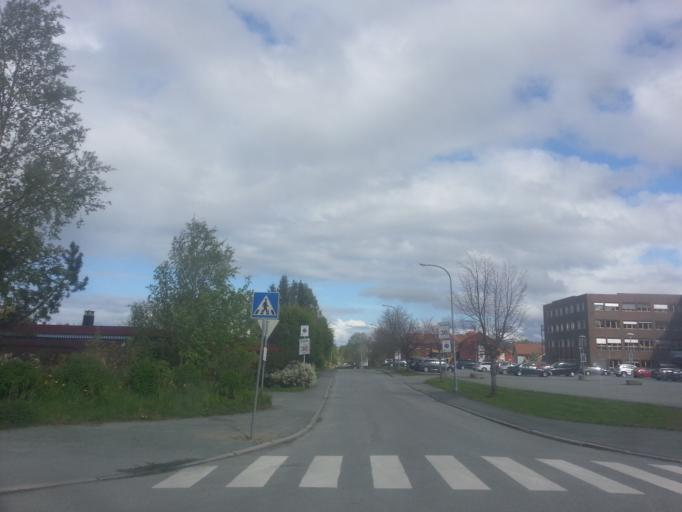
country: NO
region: Sor-Trondelag
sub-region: Trondheim
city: Trondheim
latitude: 63.4144
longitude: 10.4318
